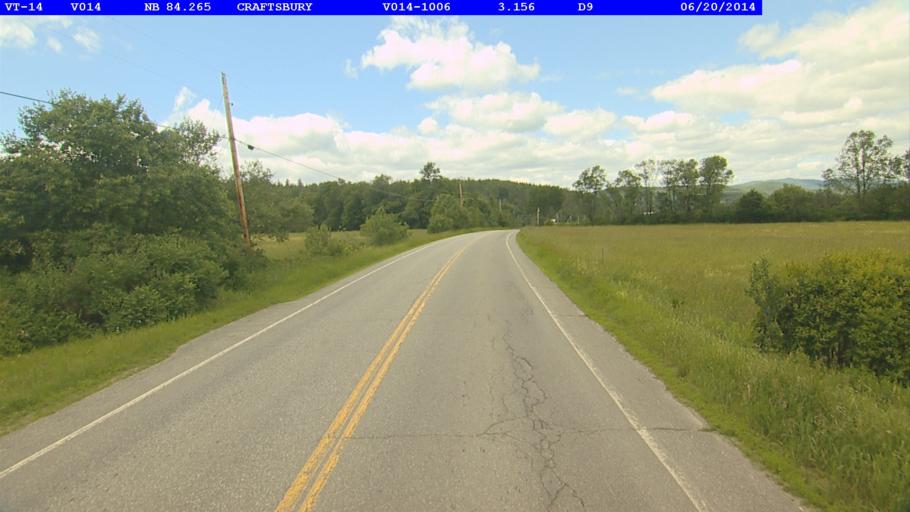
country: US
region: Vermont
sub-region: Caledonia County
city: Hardwick
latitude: 44.6371
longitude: -72.3982
